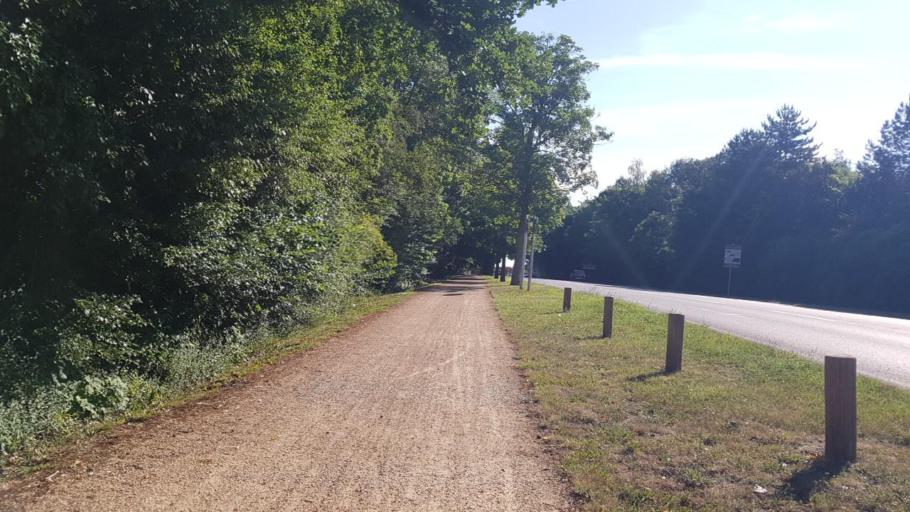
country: FR
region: Picardie
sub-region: Departement de l'Oise
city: Chamant
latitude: 49.2196
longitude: 2.6043
